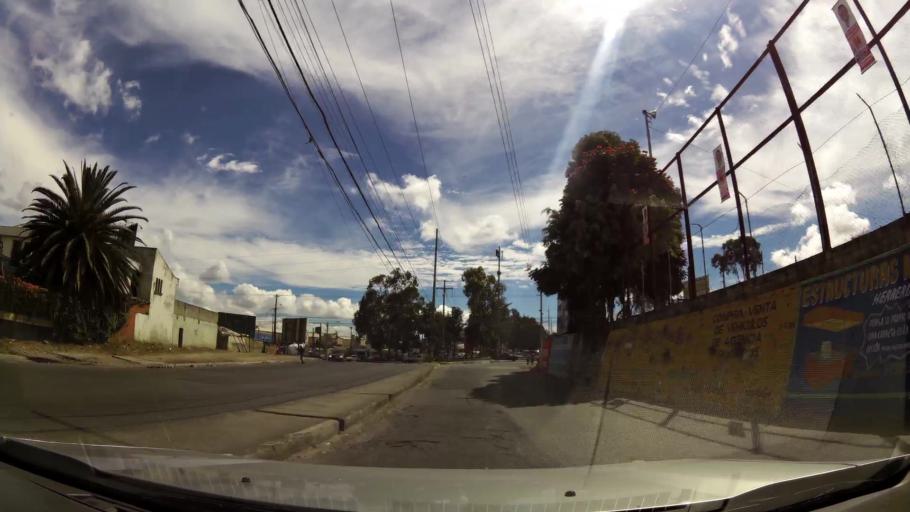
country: GT
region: Guatemala
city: Mixco
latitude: 14.6576
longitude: -90.5697
